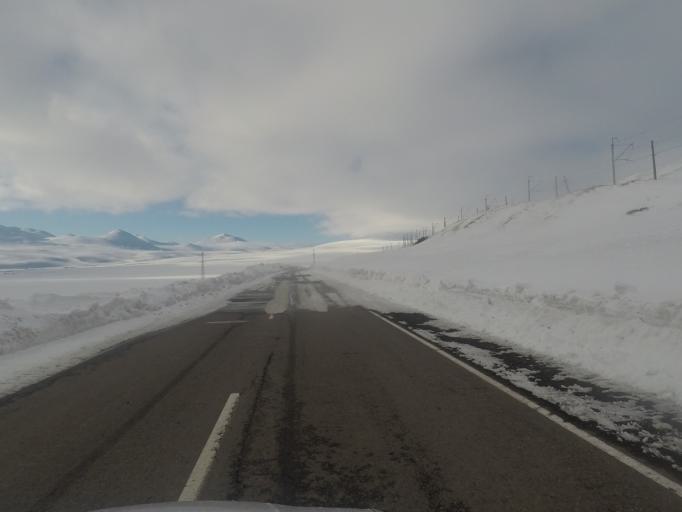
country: GE
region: Kvemo Kartli
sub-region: Tsalka
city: Tsalka
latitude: 41.4714
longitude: 43.8542
